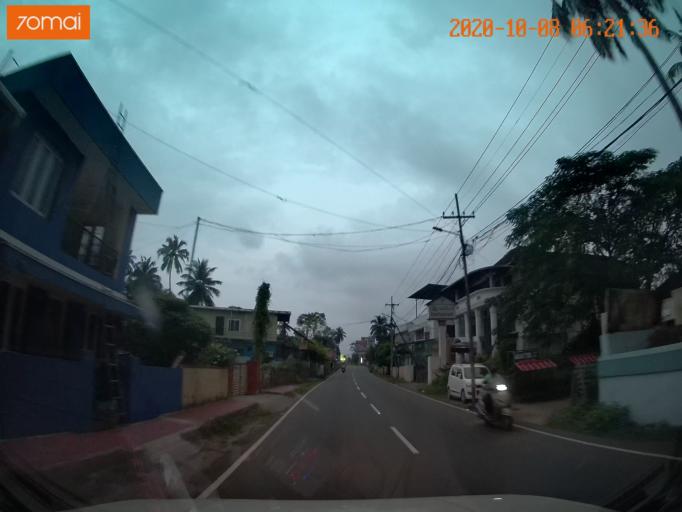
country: IN
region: Kerala
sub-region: Thrissur District
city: Trichur
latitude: 10.5214
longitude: 76.2303
